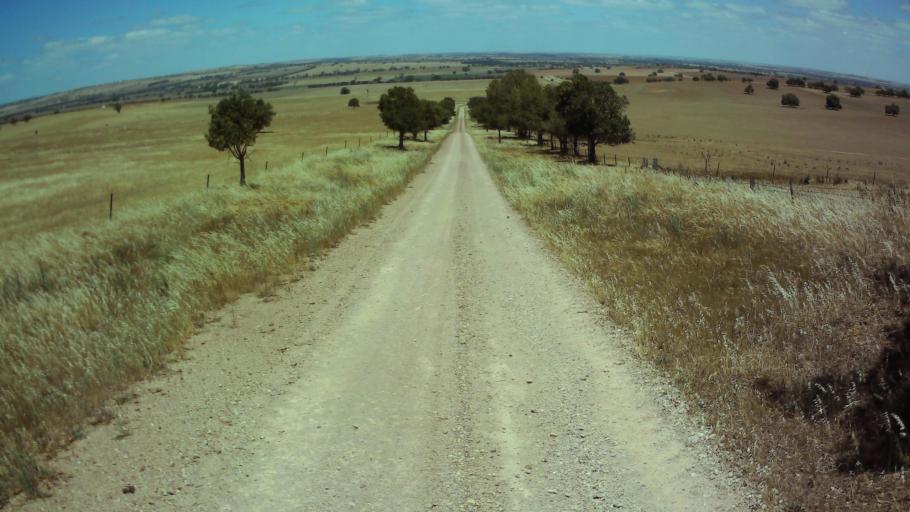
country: AU
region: New South Wales
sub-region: Weddin
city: Grenfell
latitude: -33.9589
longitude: 148.3650
